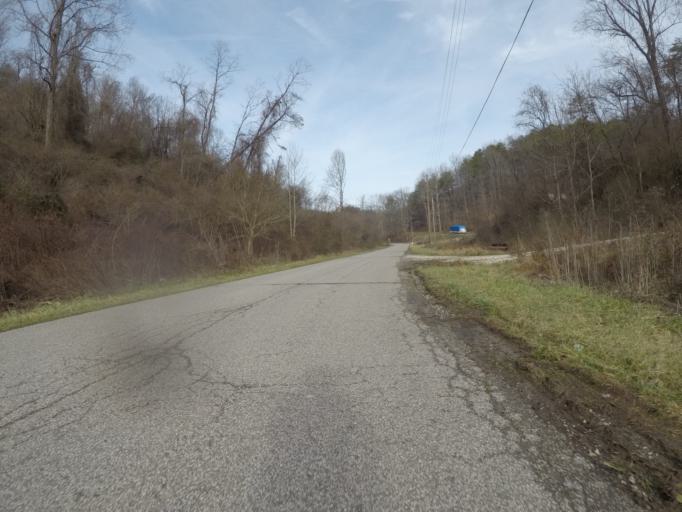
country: US
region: West Virginia
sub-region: Wayne County
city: Lavalette
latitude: 38.3497
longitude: -82.3732
